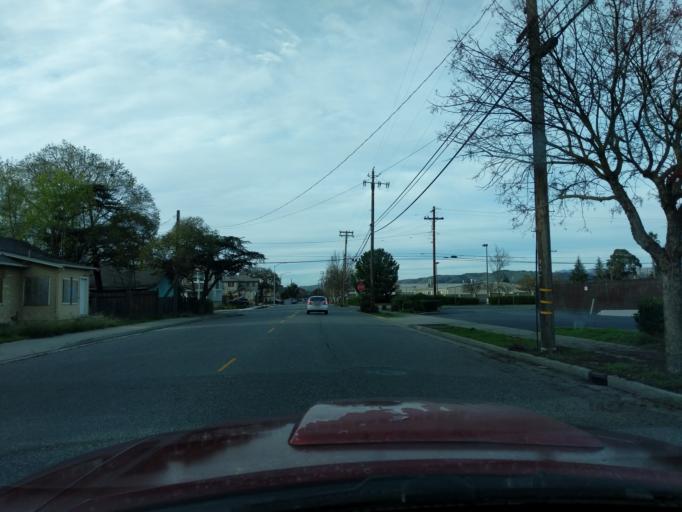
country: US
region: California
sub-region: Santa Clara County
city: Morgan Hill
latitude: 37.1211
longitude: -121.6458
